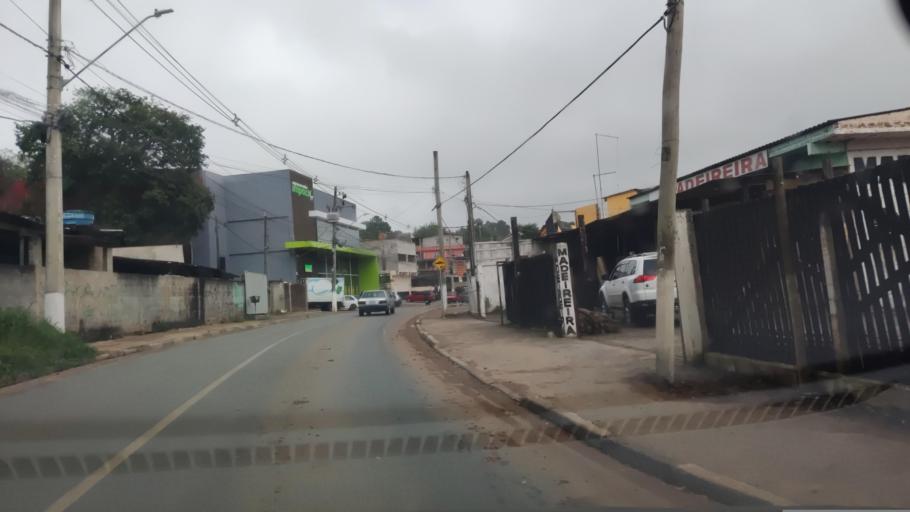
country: BR
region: Sao Paulo
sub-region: Vargem Grande Paulista
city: Vargem Grande Paulista
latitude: -23.6643
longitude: -47.0466
